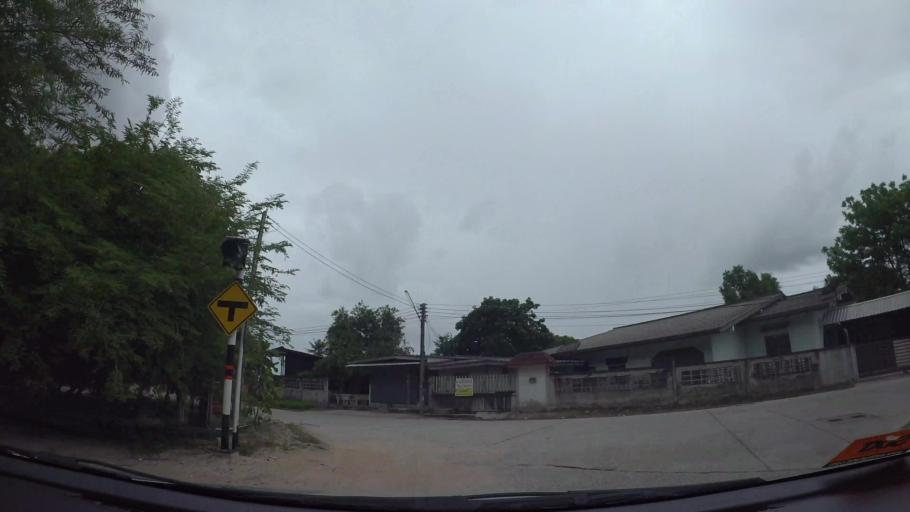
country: TH
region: Chon Buri
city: Si Racha
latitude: 13.1672
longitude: 100.9826
